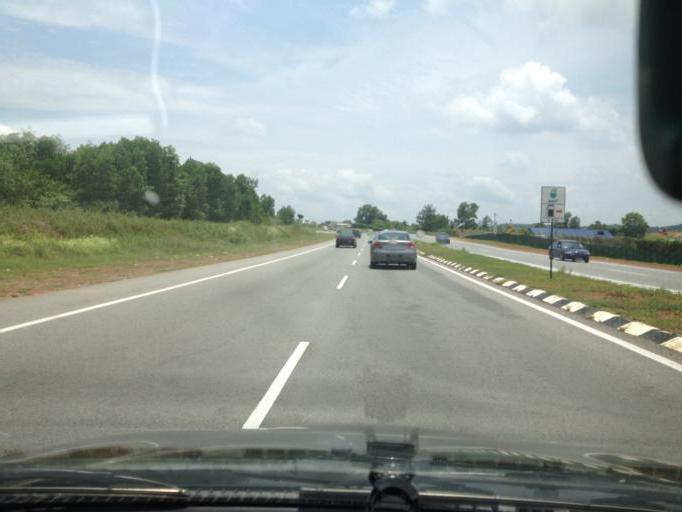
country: MY
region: Kedah
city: Sungai Petani
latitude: 5.6191
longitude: 100.5430
